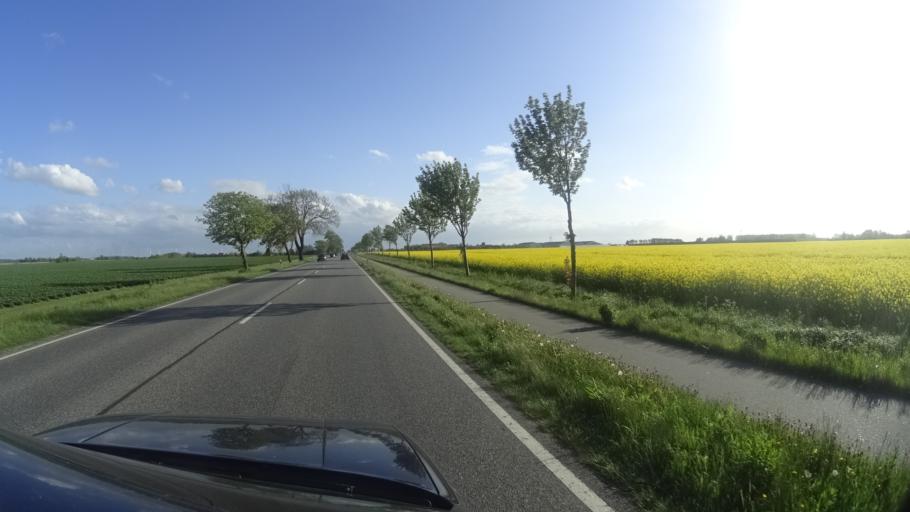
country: DE
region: Mecklenburg-Vorpommern
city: Rovershagen
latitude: 54.1682
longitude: 12.2384
